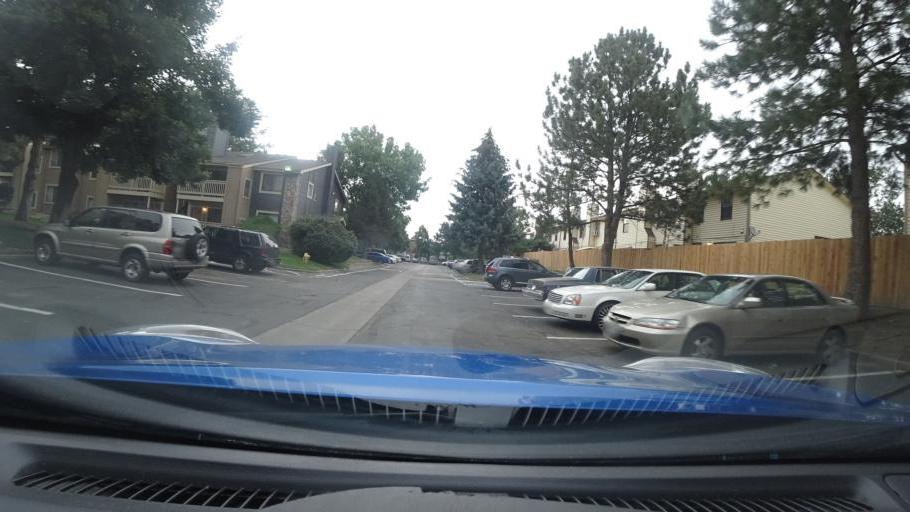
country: US
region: Colorado
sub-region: Adams County
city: Aurora
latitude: 39.6953
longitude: -104.8214
